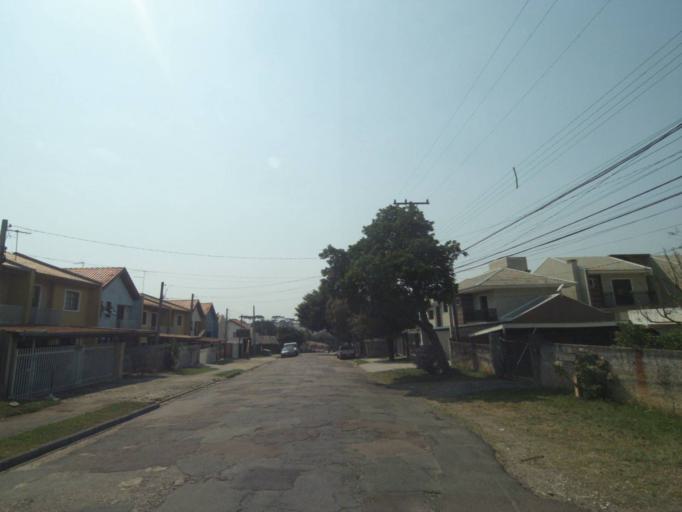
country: BR
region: Parana
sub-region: Sao Jose Dos Pinhais
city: Sao Jose dos Pinhais
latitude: -25.5228
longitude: -49.2508
